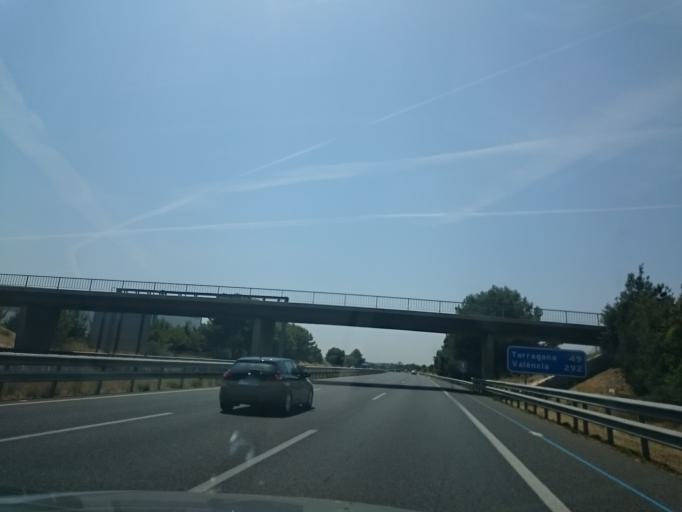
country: ES
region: Catalonia
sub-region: Provincia de Barcelona
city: Vilafranca del Penedes
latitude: 41.3286
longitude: 1.6543
